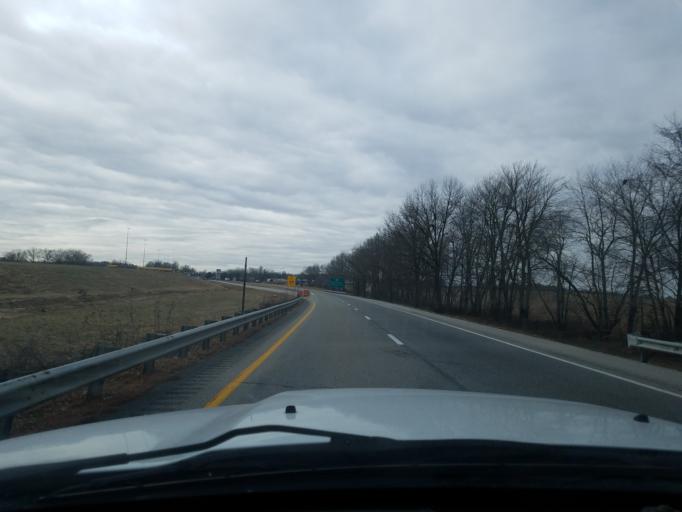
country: US
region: Kentucky
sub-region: Ohio County
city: Beaver Dam
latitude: 37.3791
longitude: -86.8230
